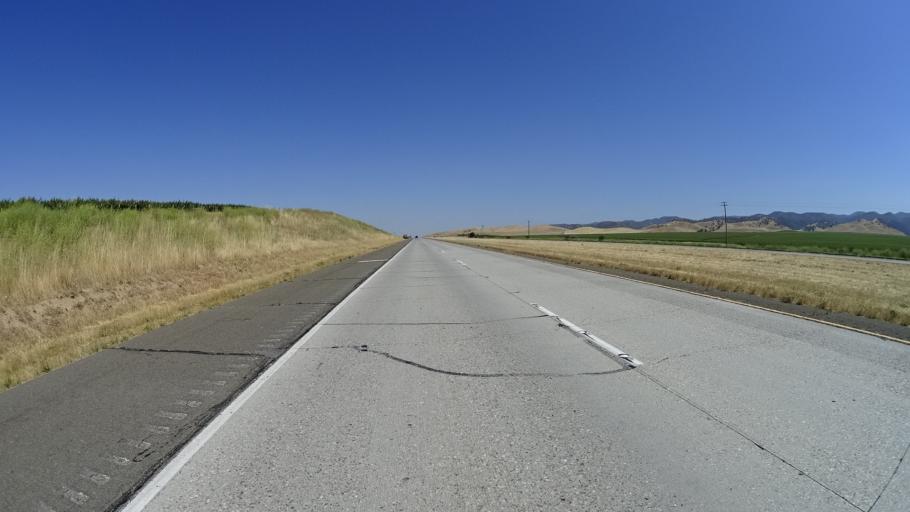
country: US
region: California
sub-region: Monterey County
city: King City
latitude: 36.0684
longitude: -120.9869
